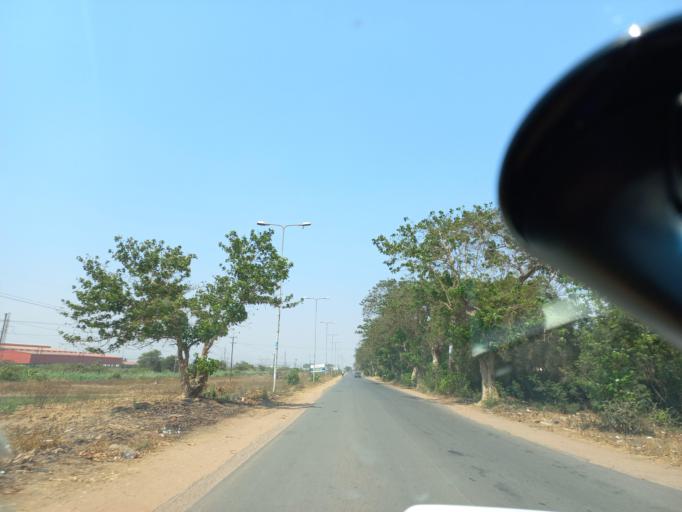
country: ZM
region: Lusaka
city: Kafue
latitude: -15.7454
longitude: 28.1678
